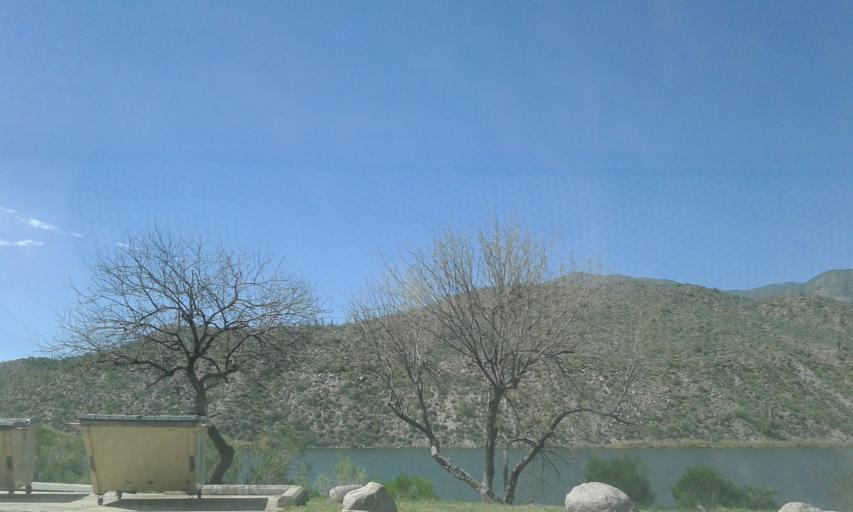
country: US
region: Arizona
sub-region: Gila County
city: Tonto Basin
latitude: 33.6285
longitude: -111.2068
